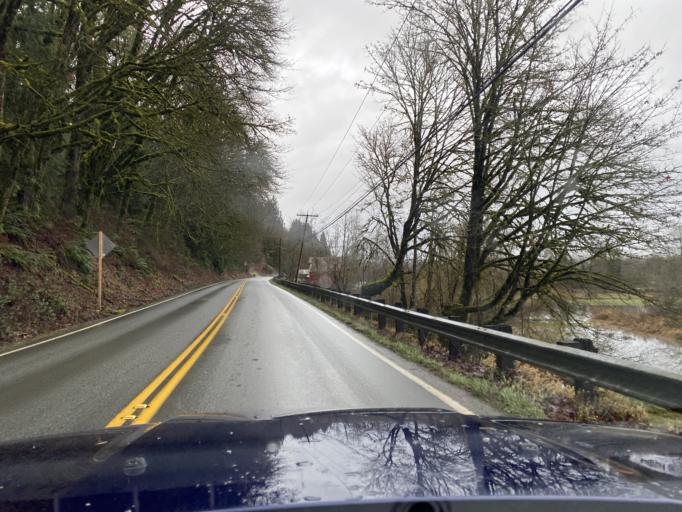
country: US
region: Washington
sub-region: King County
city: Duvall
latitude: 47.7179
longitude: -122.0084
